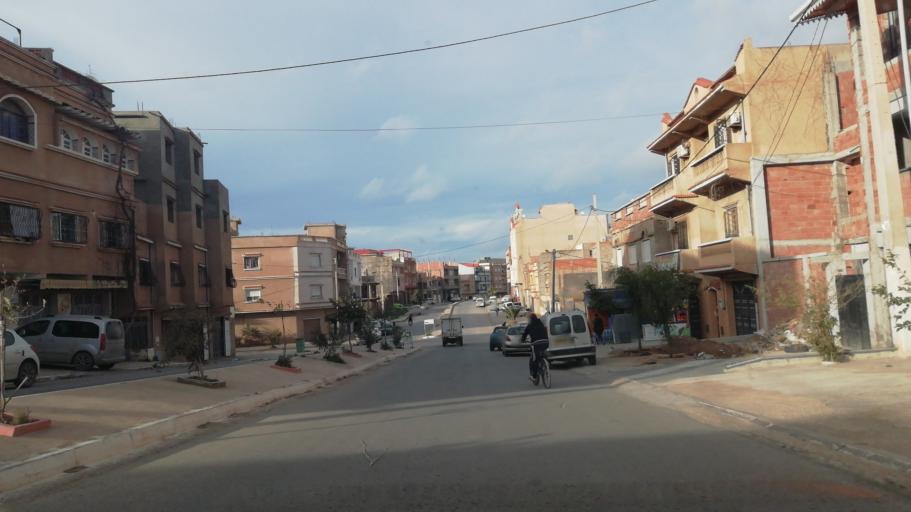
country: DZ
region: Oran
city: Bir el Djir
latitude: 35.7334
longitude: -0.5726
